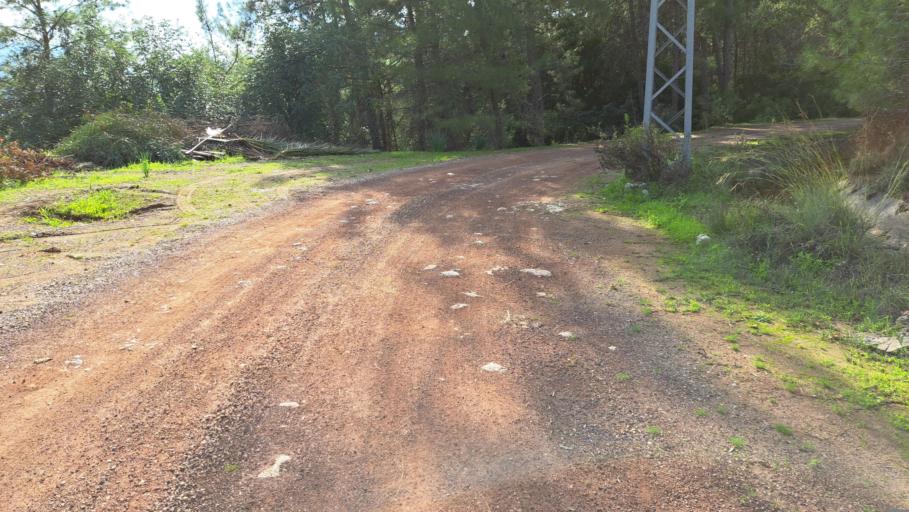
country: TR
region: Antalya
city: Tekirova
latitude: 36.3963
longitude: 30.4309
